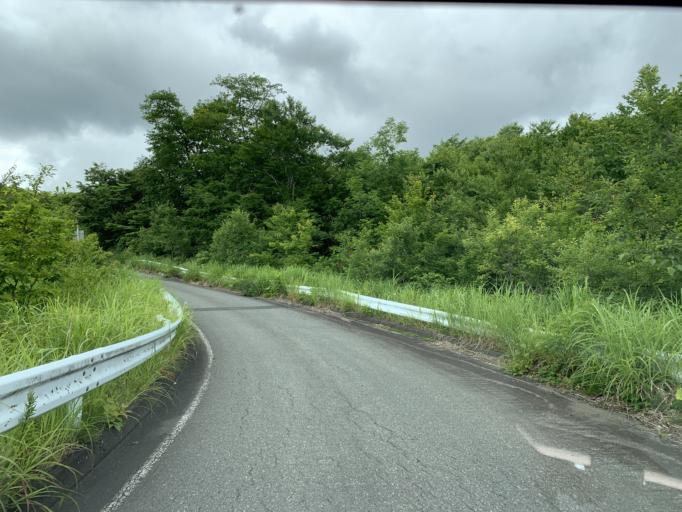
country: JP
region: Iwate
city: Ichinoseki
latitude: 38.9340
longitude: 140.8828
